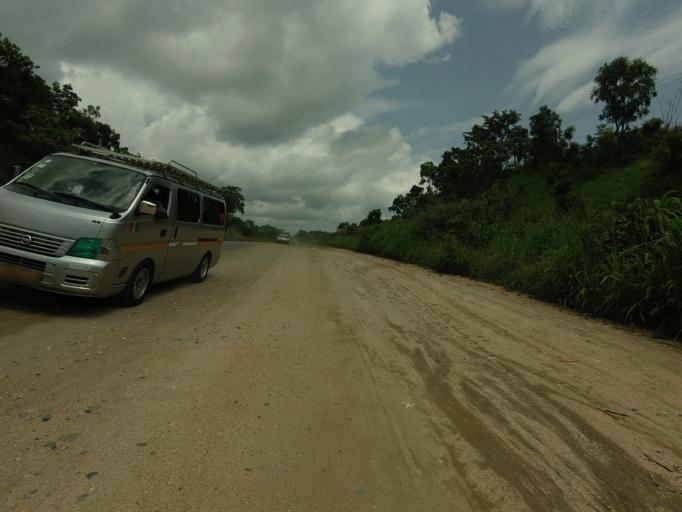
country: GH
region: Volta
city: Ho
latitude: 6.6729
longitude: 0.3116
